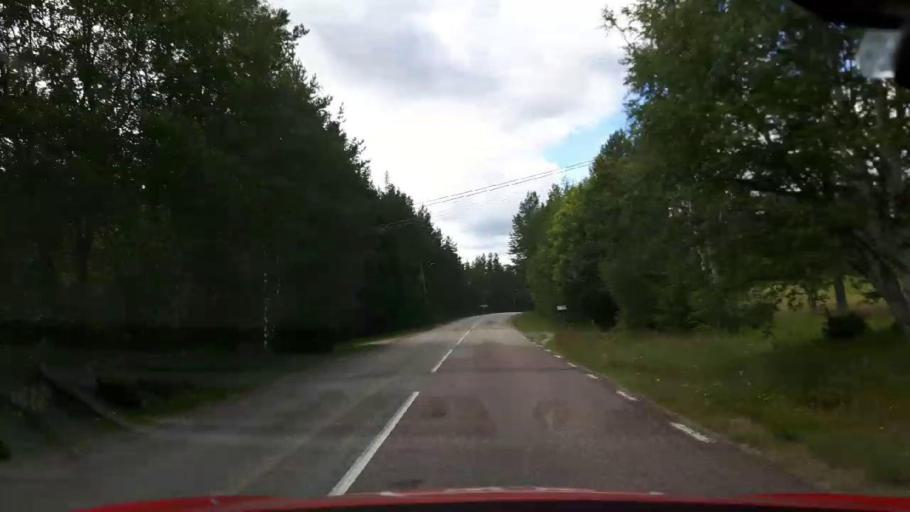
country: SE
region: Jaemtland
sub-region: Harjedalens Kommun
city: Sveg
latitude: 61.8447
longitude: 14.0463
